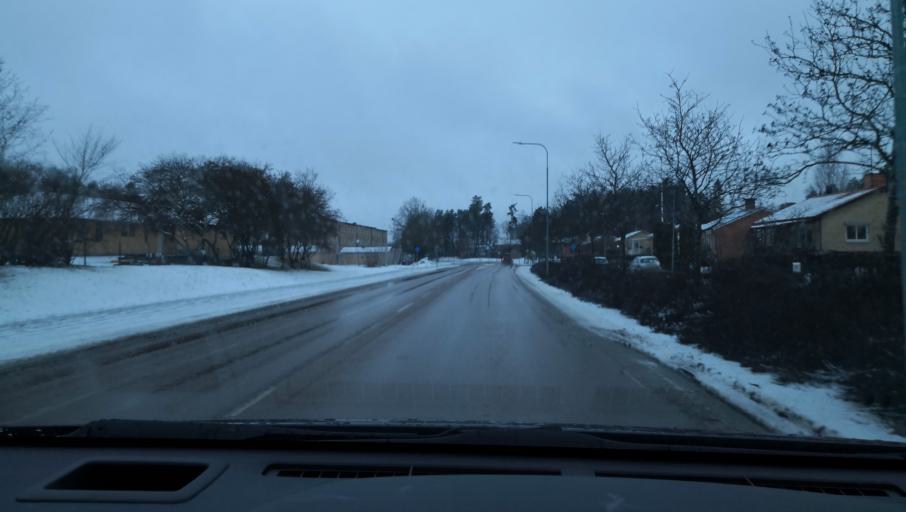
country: SE
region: Vaestmanland
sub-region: Kopings Kommun
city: Koping
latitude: 59.5213
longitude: 16.0040
